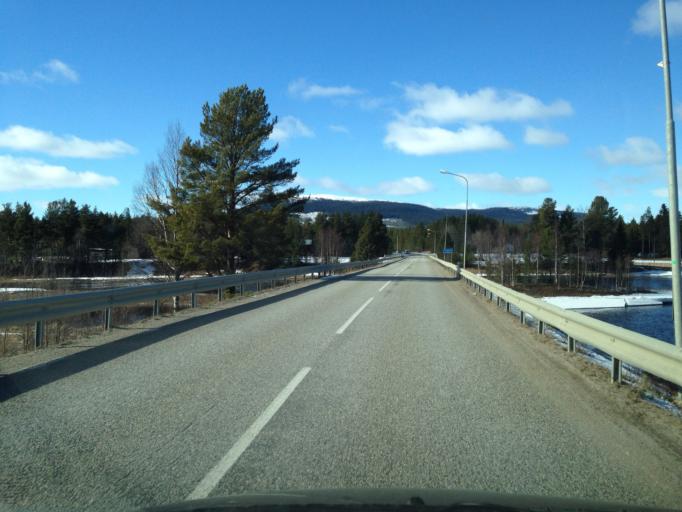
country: SE
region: Jaemtland
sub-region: Harjedalens Kommun
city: Sveg
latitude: 62.1547
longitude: 13.8764
